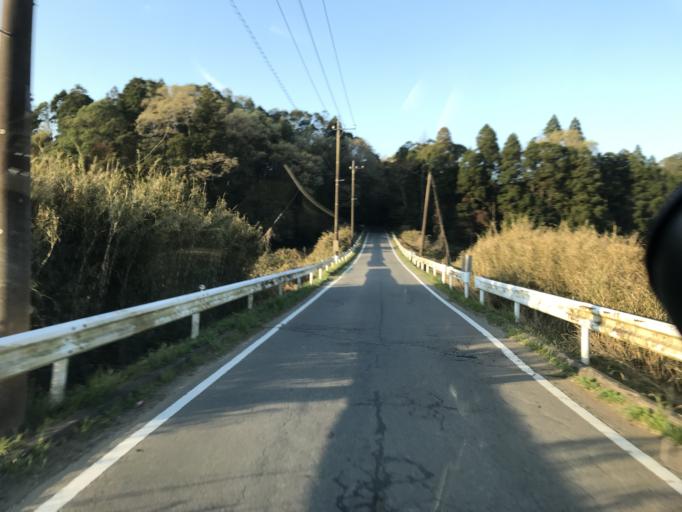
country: JP
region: Chiba
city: Yokaichiba
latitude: 35.7745
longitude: 140.5348
